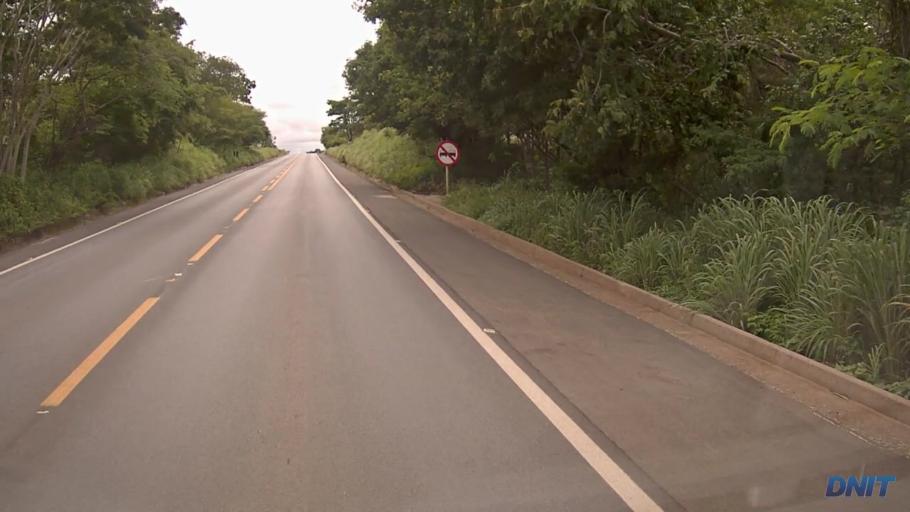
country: BR
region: Goias
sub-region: Posse
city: Posse
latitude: -14.2911
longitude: -46.4321
